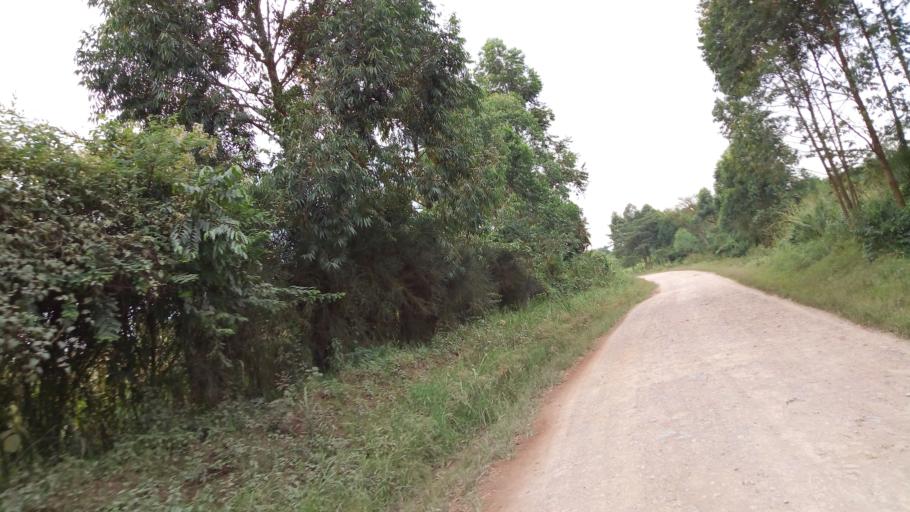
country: UG
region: Central Region
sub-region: Kiboga District
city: Kiboga
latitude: 0.7117
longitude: 31.7557
